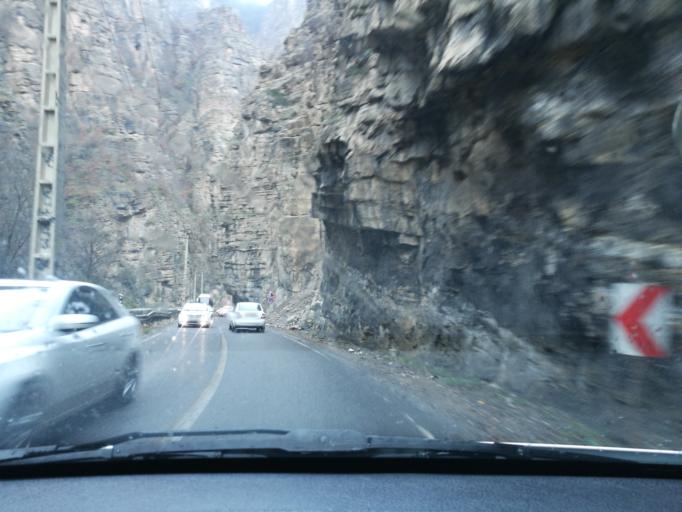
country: IR
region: Mazandaran
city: Chalus
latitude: 36.2708
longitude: 51.2473
